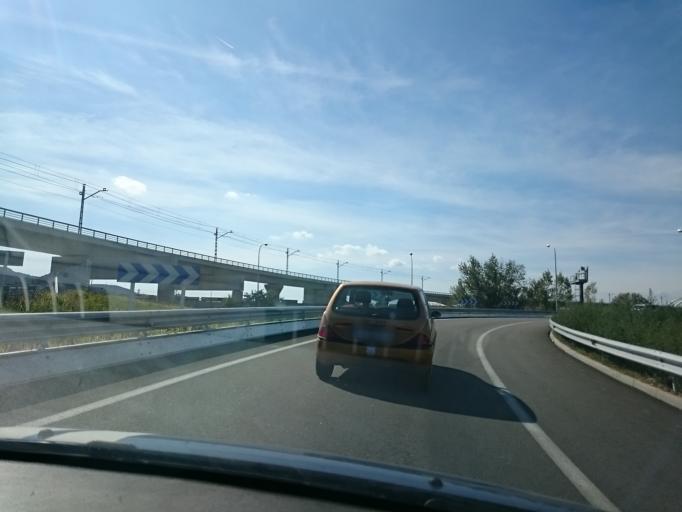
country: ES
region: Catalonia
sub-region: Provincia de Barcelona
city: Mollet del Valles
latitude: 41.5262
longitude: 2.2117
